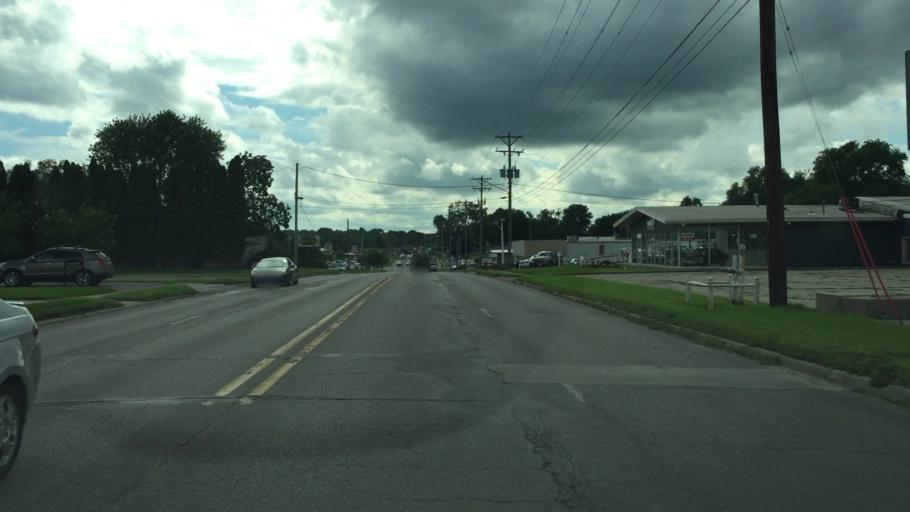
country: US
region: Iowa
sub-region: Jasper County
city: Newton
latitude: 41.6992
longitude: -93.0291
